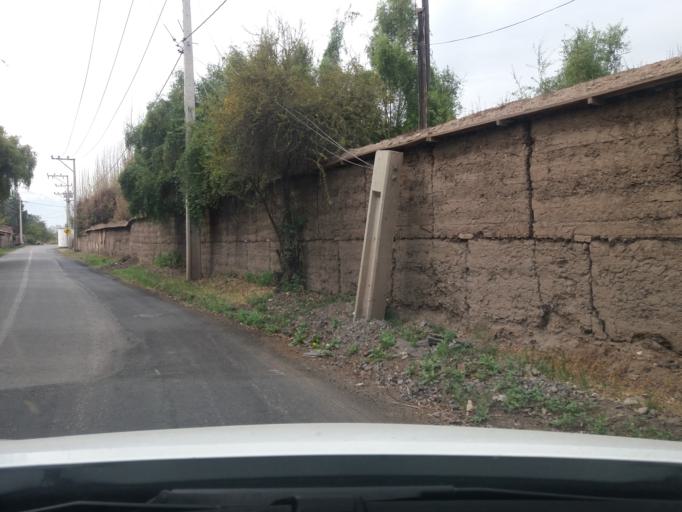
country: CL
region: Valparaiso
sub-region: Provincia de Los Andes
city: Los Andes
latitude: -32.8301
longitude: -70.6332
